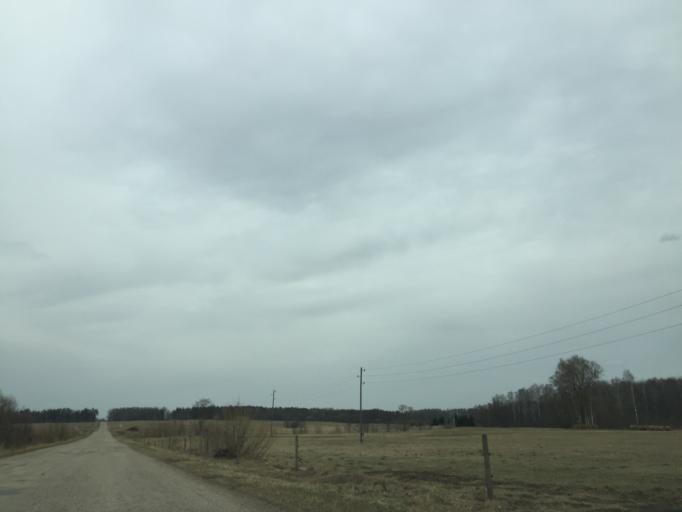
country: LV
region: Ilukste
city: Ilukste
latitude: 56.0299
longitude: 26.2753
